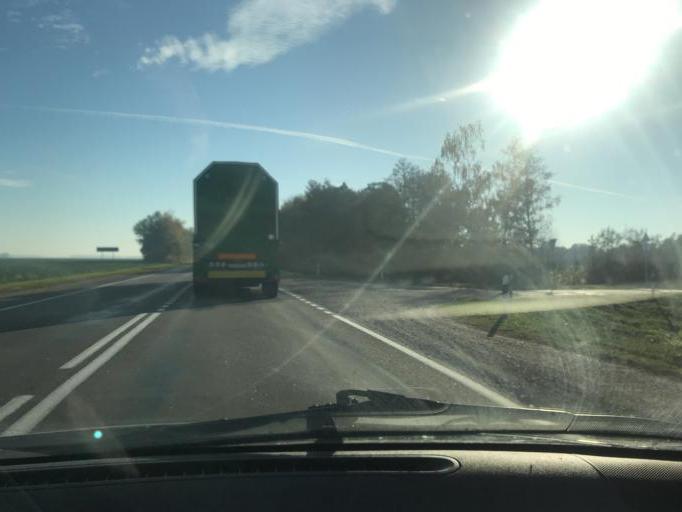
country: BY
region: Brest
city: Ivanava
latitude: 52.1508
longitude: 25.3822
